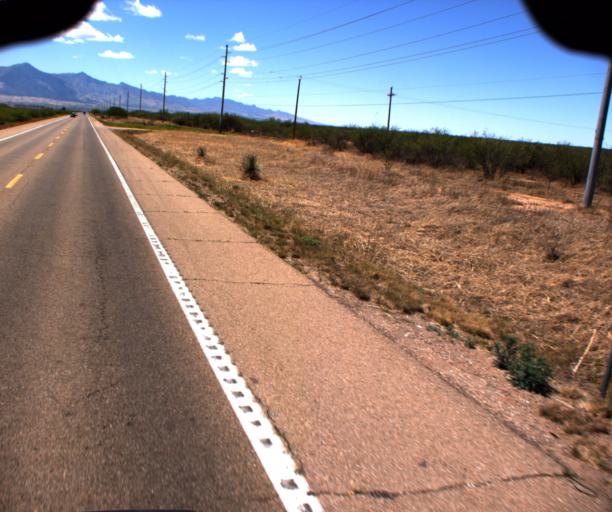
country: US
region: Arizona
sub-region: Cochise County
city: Naco
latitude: 31.3775
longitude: -110.0195
